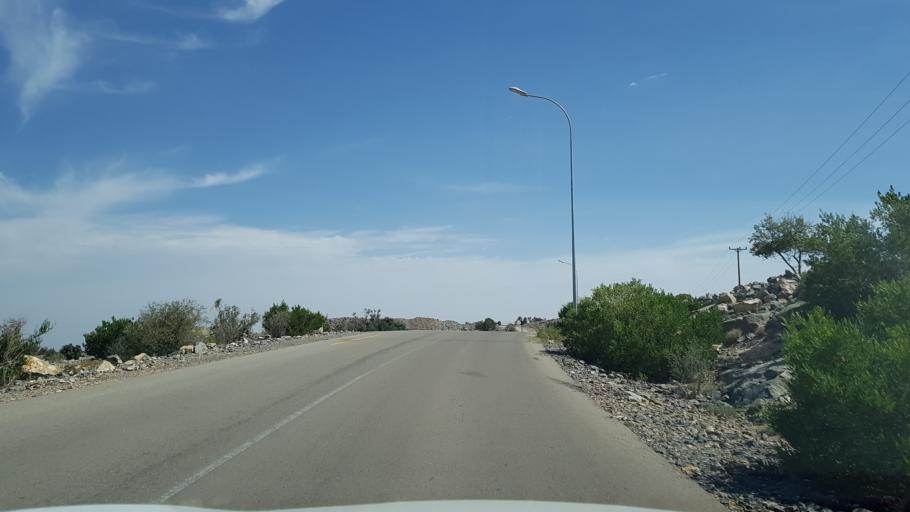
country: OM
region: Al Batinah
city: Bayt al `Awabi
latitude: 23.1207
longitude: 57.6031
